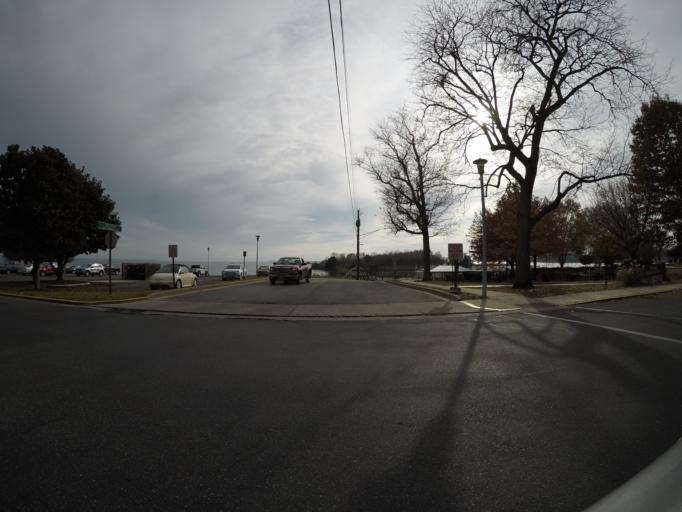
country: US
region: Maryland
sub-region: Harford County
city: Havre de Grace
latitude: 39.5389
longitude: -76.0887
